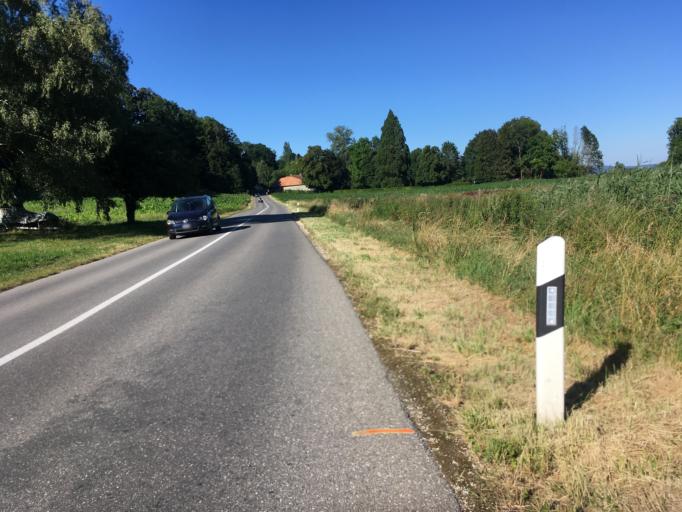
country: CH
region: Vaud
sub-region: Broye-Vully District
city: Avenches
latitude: 46.9358
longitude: 7.0535
